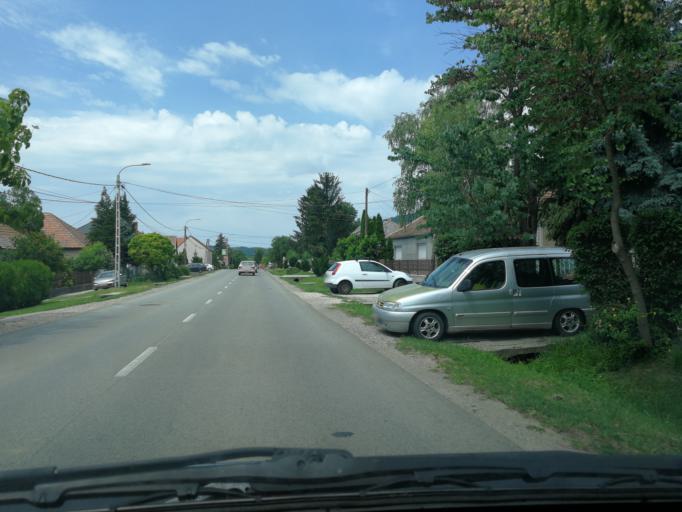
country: HU
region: Baranya
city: Siklos
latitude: 45.8706
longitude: 18.2739
